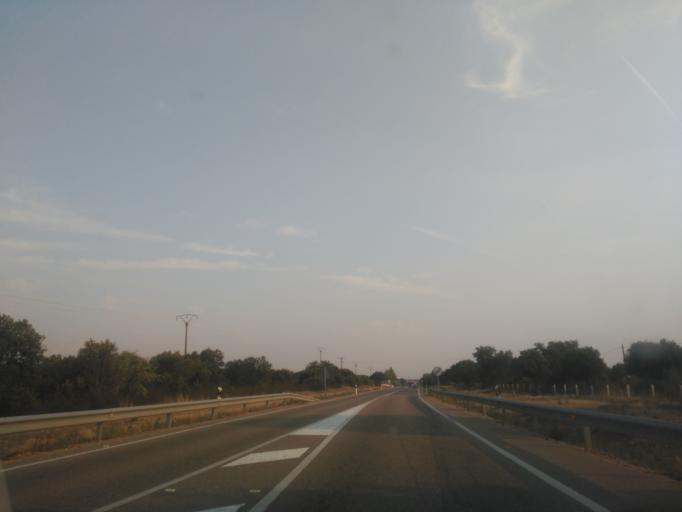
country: ES
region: Castille and Leon
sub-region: Provincia de Zamora
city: San Cebrian de Castro
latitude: 41.7134
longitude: -5.8089
